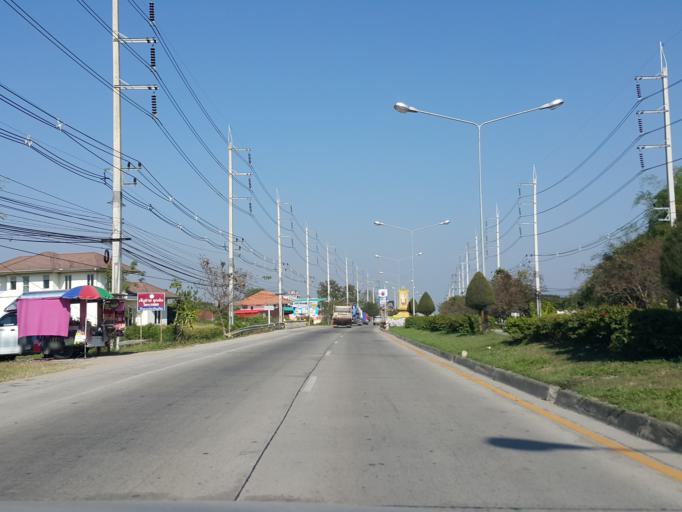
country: TH
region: Chiang Mai
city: San Sai
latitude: 18.8308
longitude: 99.0537
